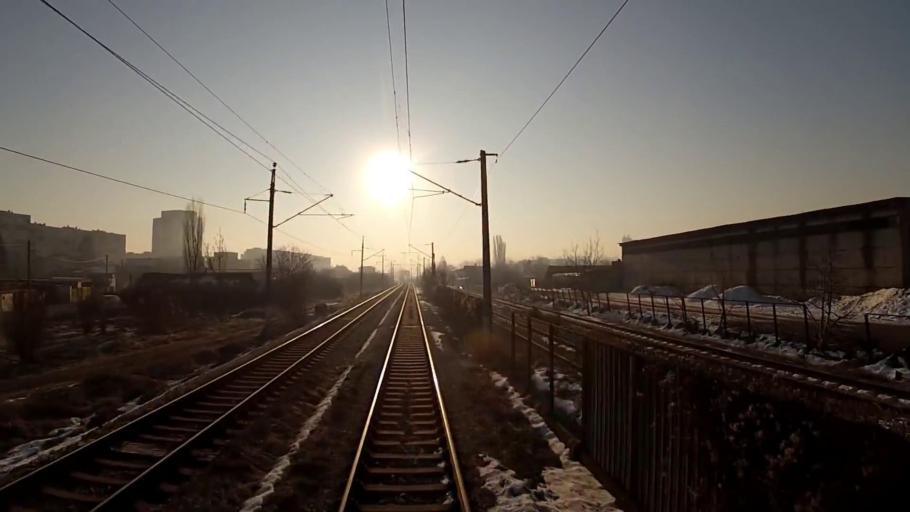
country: BG
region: Sofia-Capital
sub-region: Stolichna Obshtina
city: Sofia
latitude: 42.7321
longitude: 23.2728
